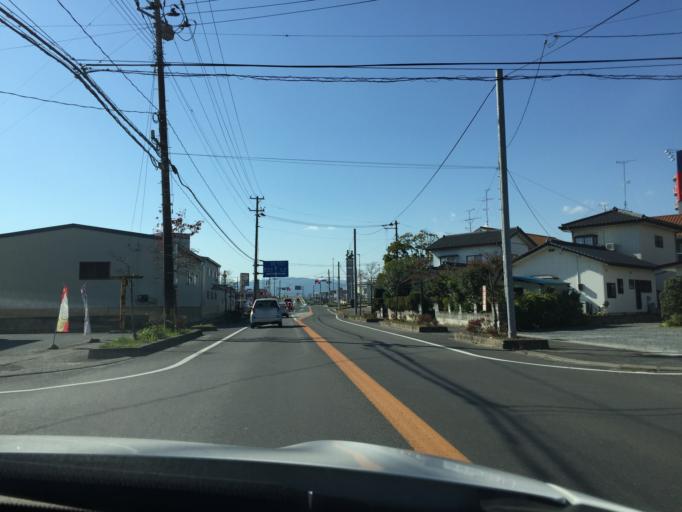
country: JP
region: Miyagi
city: Marumori
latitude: 37.8027
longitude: 140.9299
